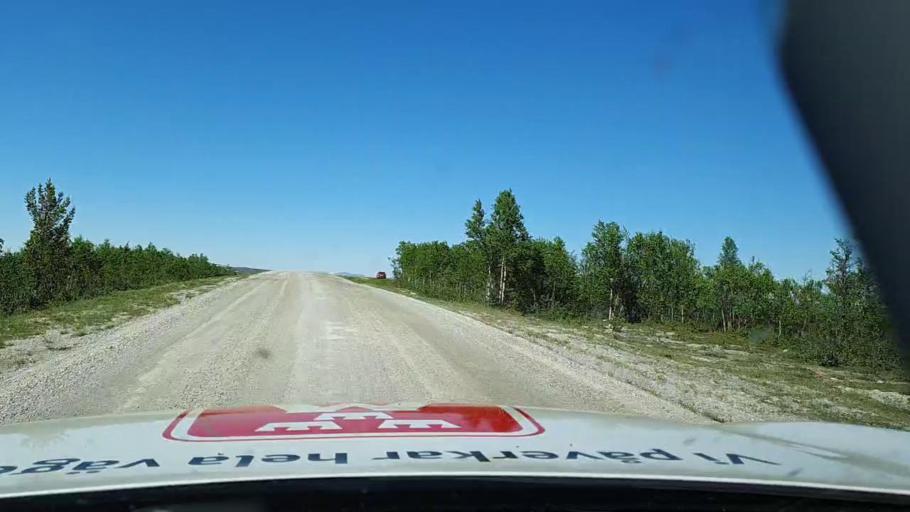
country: SE
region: Jaemtland
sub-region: Are Kommun
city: Are
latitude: 62.6491
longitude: 12.6630
